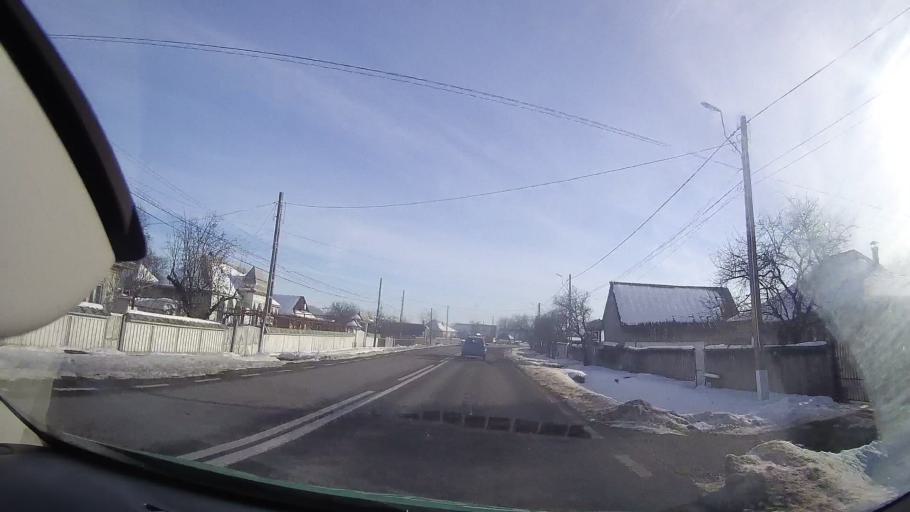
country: RO
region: Neamt
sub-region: Comuna Cracaoani
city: Cracaoani
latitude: 47.0924
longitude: 26.3211
